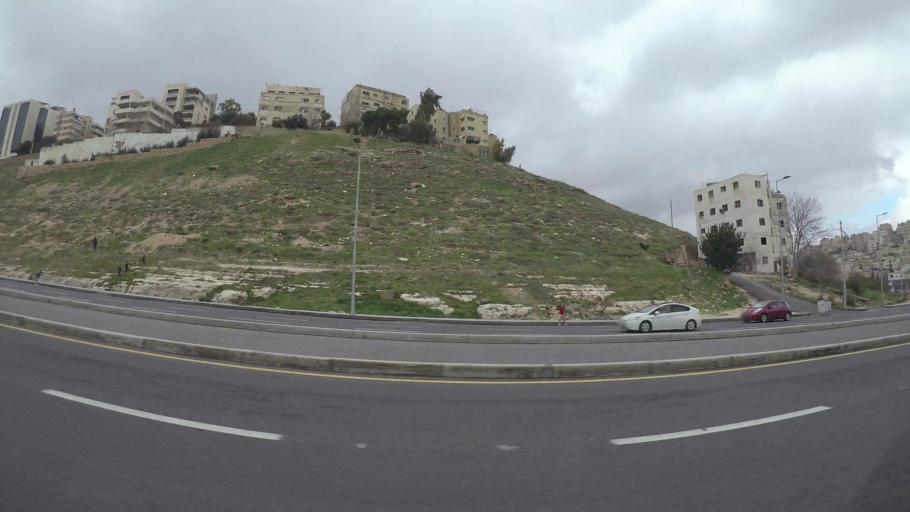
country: JO
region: Amman
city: Amman
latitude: 31.9463
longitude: 35.9052
